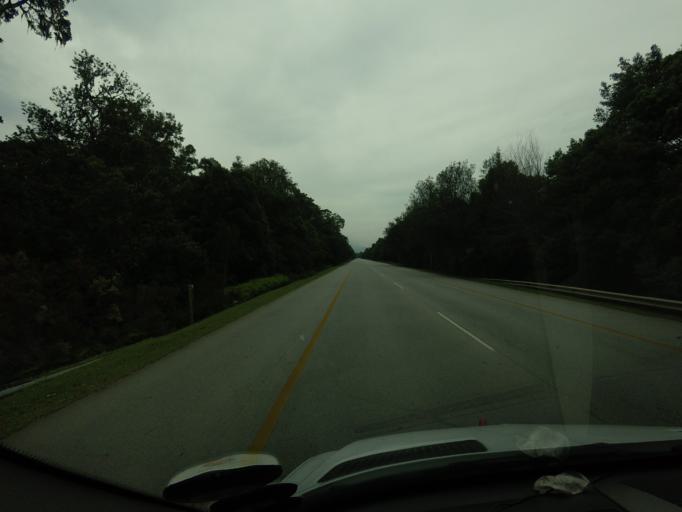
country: ZA
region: Eastern Cape
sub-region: Cacadu District Municipality
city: Kareedouw
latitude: -33.9704
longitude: 23.8463
